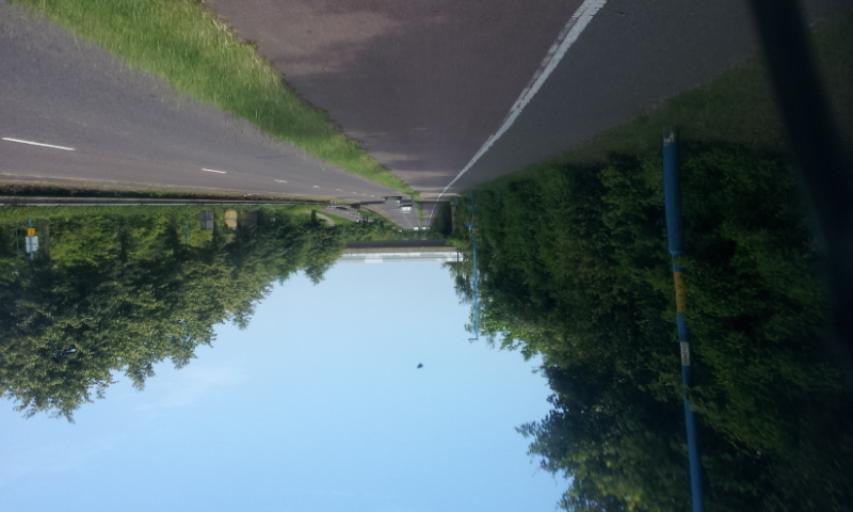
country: GB
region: England
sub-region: Kent
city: Gillingham
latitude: 51.3812
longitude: 0.5753
